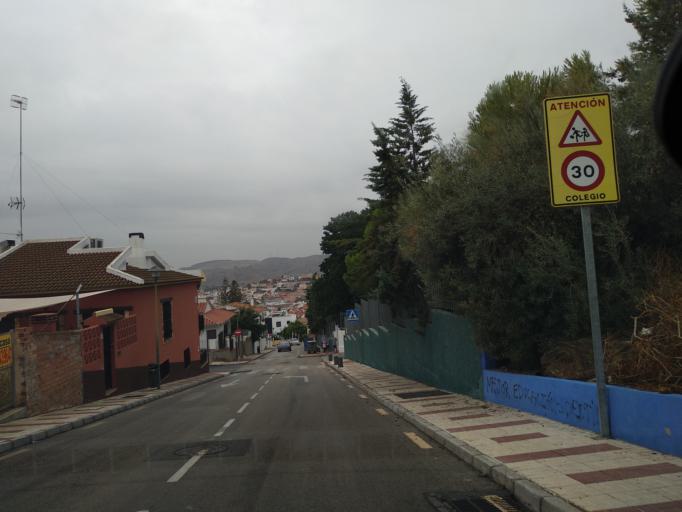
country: ES
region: Andalusia
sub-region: Provincia de Malaga
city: Malaga
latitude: 36.7401
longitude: -4.4753
